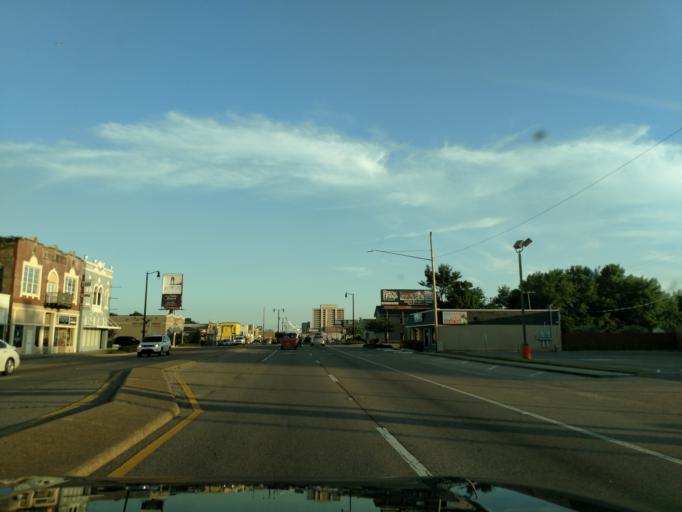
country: US
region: Mississippi
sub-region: Harrison County
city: Gulfport
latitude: 30.3775
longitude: -89.0931
